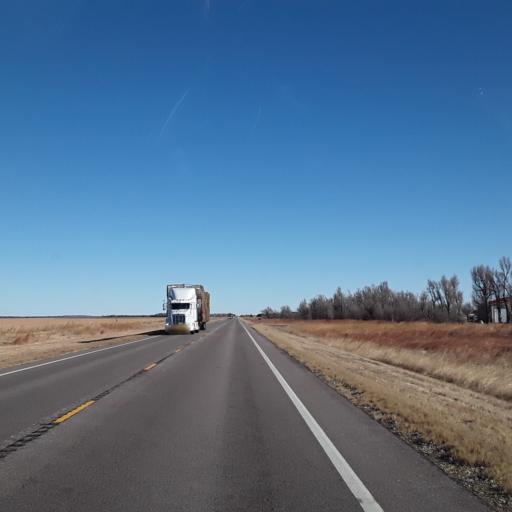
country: US
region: Kansas
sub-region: Pawnee County
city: Larned
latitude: 38.0955
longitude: -99.2146
